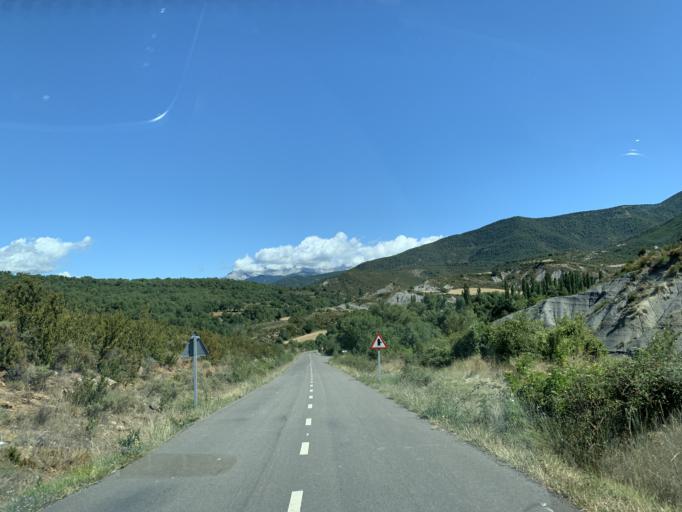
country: ES
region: Aragon
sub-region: Provincia de Huesca
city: Sabinanigo
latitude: 42.5333
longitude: -0.3232
